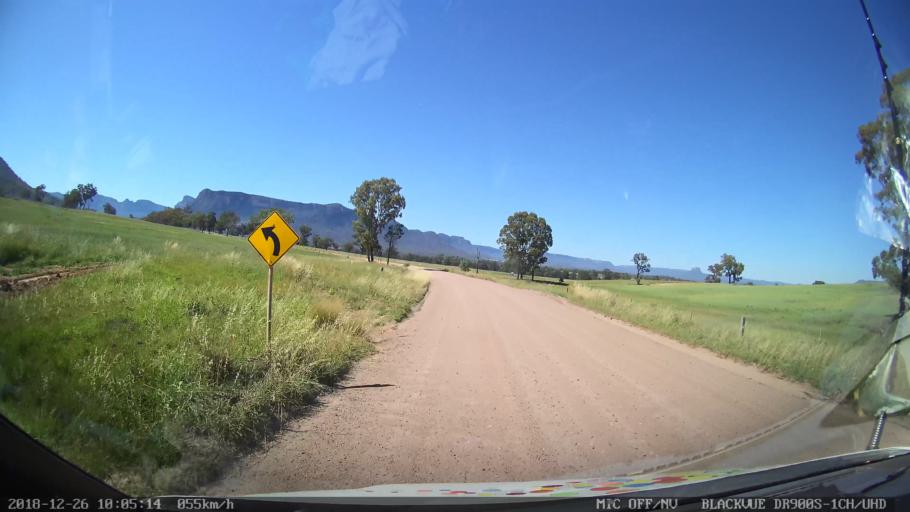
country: AU
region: New South Wales
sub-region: Mid-Western Regional
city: Kandos
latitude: -33.0765
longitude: 150.2119
